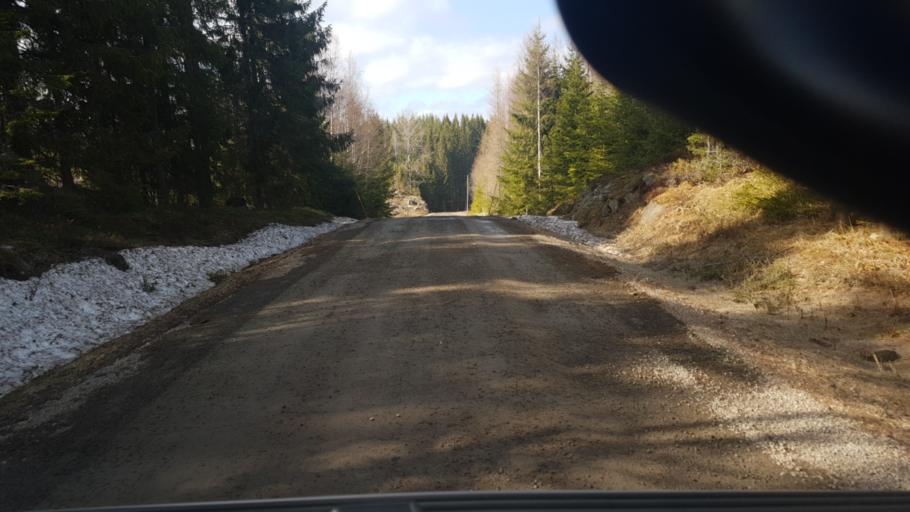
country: SE
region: Vaermland
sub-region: Eda Kommun
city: Amotfors
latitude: 59.8062
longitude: 12.4432
